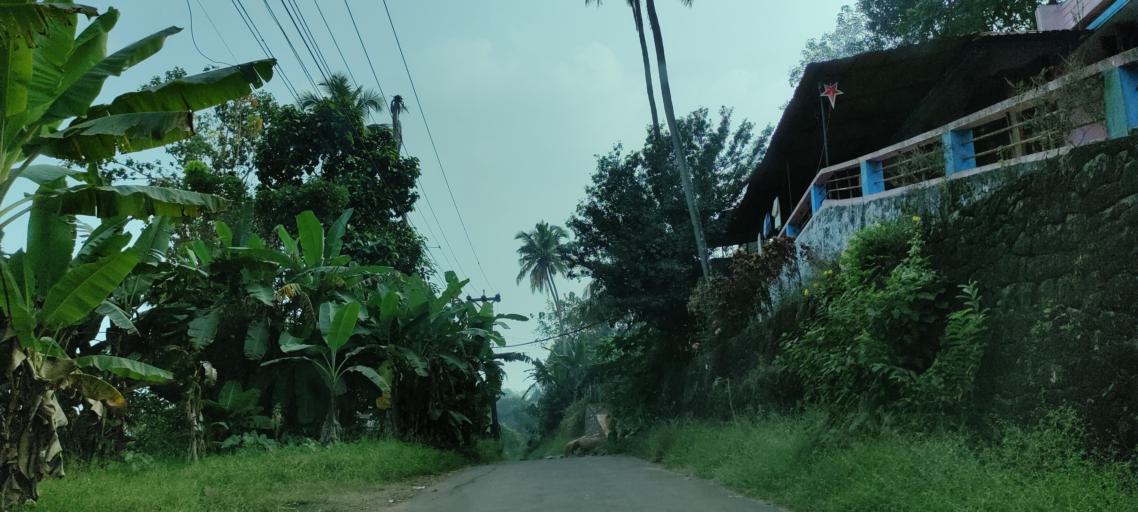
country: IN
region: Kerala
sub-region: Ernakulam
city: Piravam
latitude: 9.8017
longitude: 76.5355
